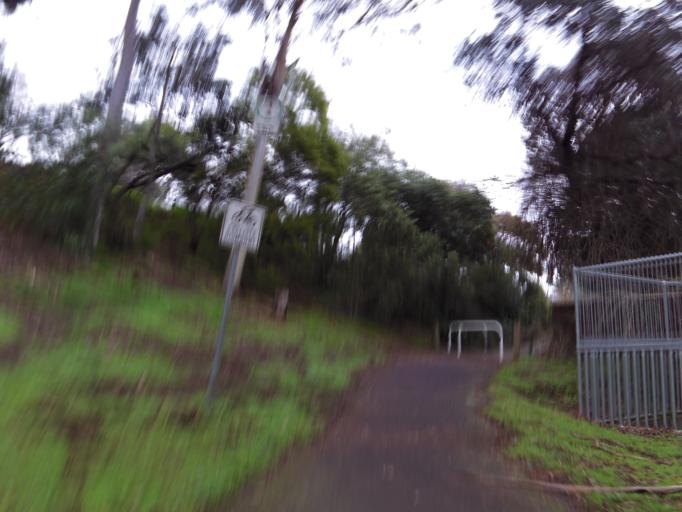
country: AU
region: Victoria
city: Alphington
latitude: -37.7689
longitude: 145.0370
